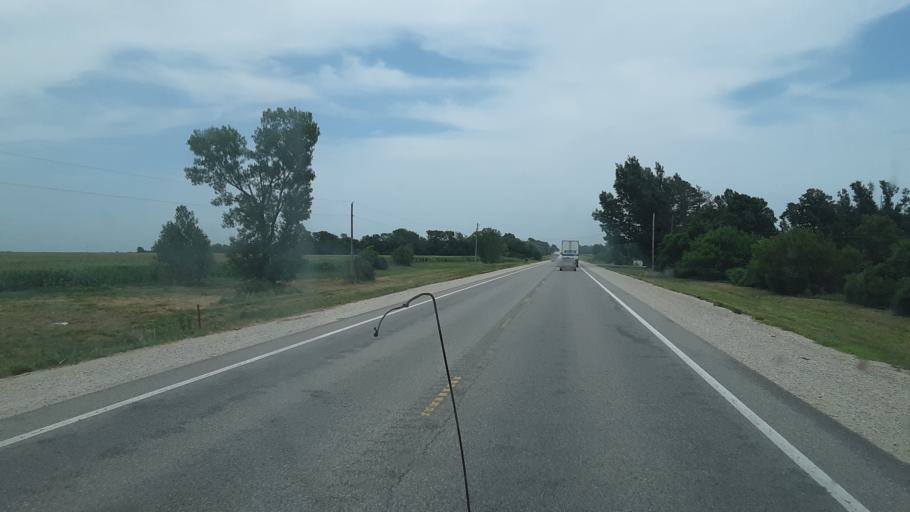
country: US
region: Kansas
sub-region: Allen County
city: Iola
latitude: 37.9217
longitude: -95.1966
